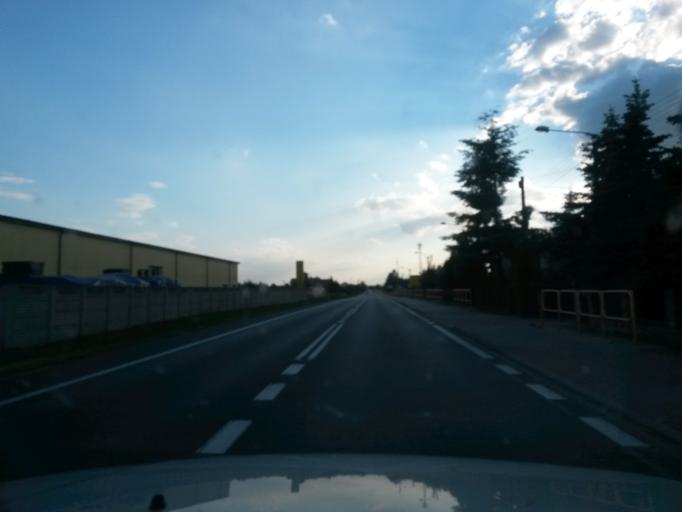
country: PL
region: Lodz Voivodeship
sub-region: Powiat belchatowski
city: Rusiec
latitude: 51.3227
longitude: 18.9801
